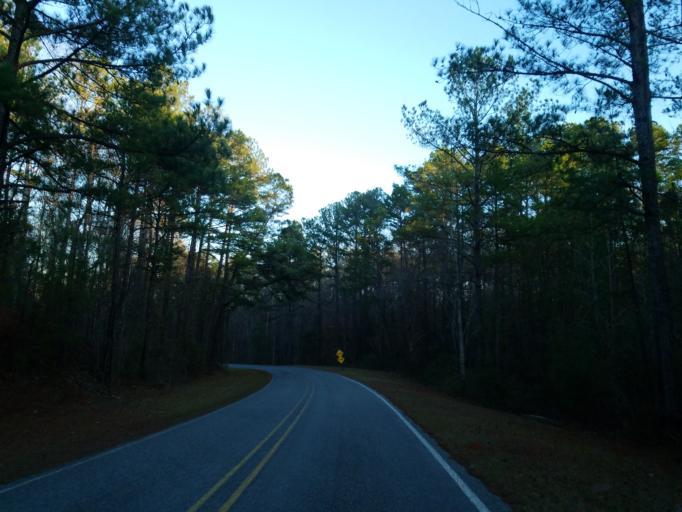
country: US
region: Mississippi
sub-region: Clarke County
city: Stonewall
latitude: 32.2630
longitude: -88.7969
